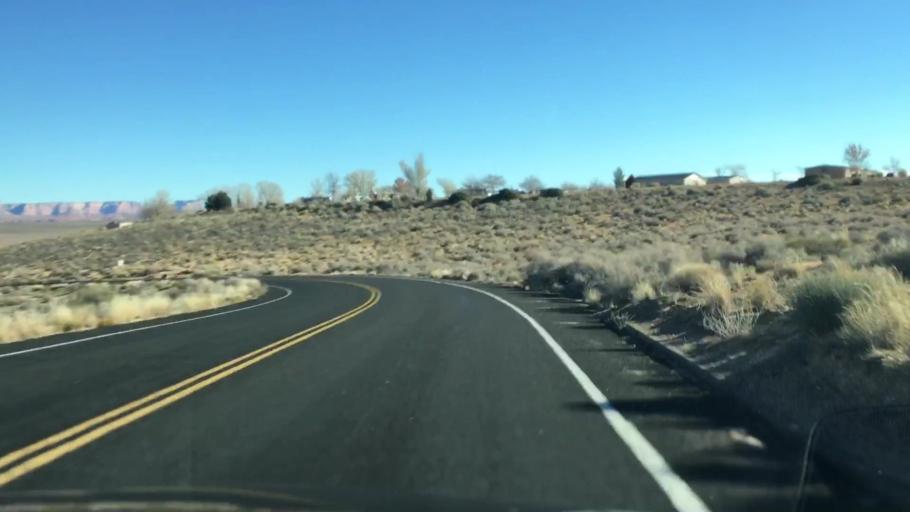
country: US
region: Arizona
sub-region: Coconino County
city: Page
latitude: 36.9936
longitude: -111.4977
